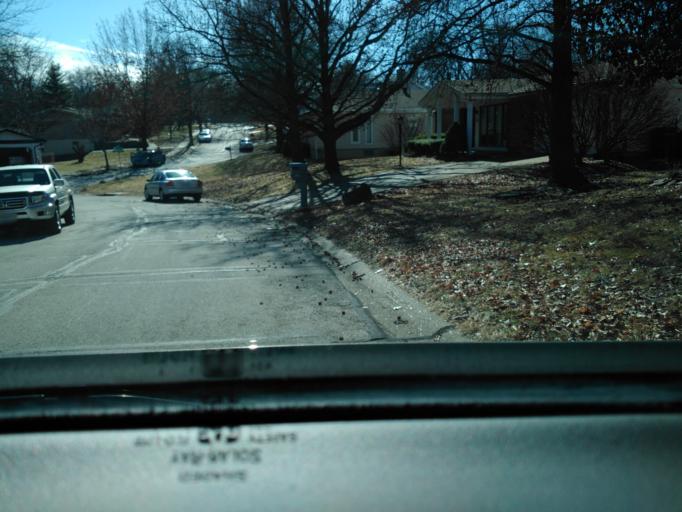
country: US
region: Missouri
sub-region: Saint Louis County
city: Ballwin
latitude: 38.5996
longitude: -90.5476
